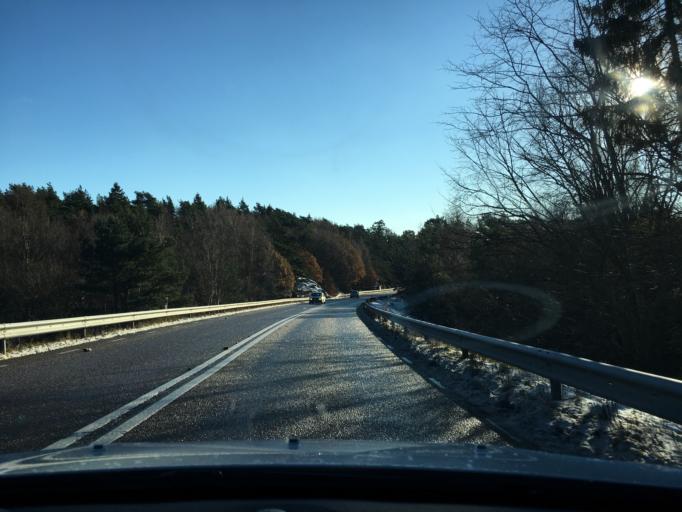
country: SE
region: Vaestra Goetaland
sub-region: Tjorns Kommun
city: Myggenas
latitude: 58.0798
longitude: 11.6956
